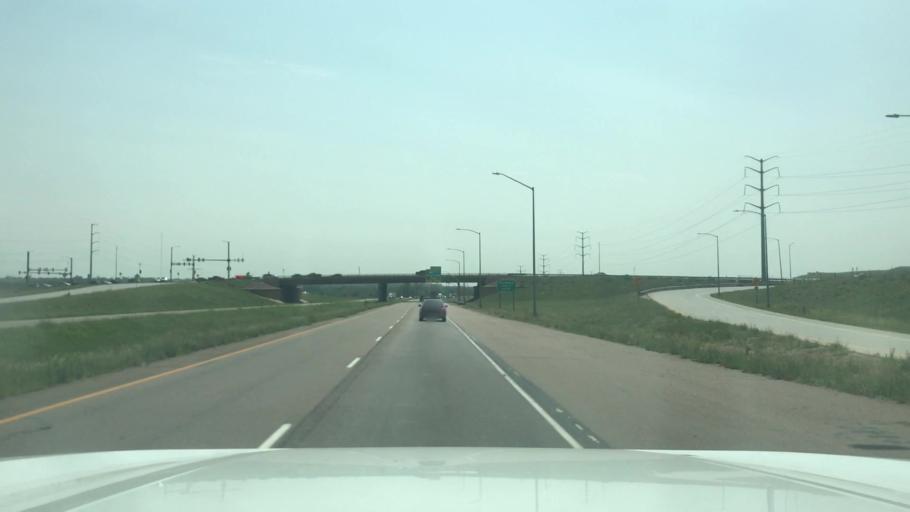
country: US
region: Colorado
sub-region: El Paso County
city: Security-Widefield
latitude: 38.7269
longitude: -104.7352
